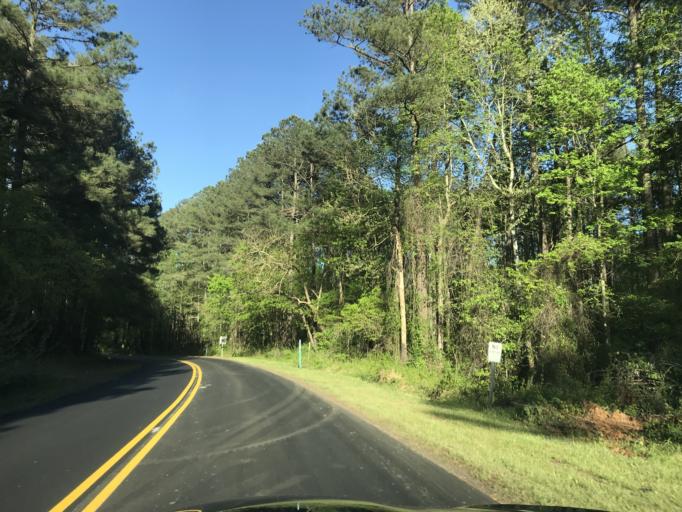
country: US
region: North Carolina
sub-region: Wake County
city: Raleigh
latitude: 35.8444
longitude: -78.5667
